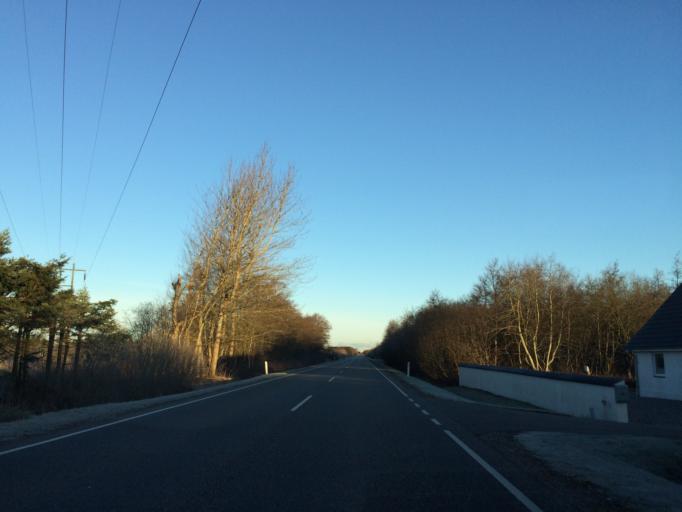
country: DK
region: Central Jutland
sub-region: Holstebro Kommune
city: Ulfborg
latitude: 56.3764
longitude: 8.3297
